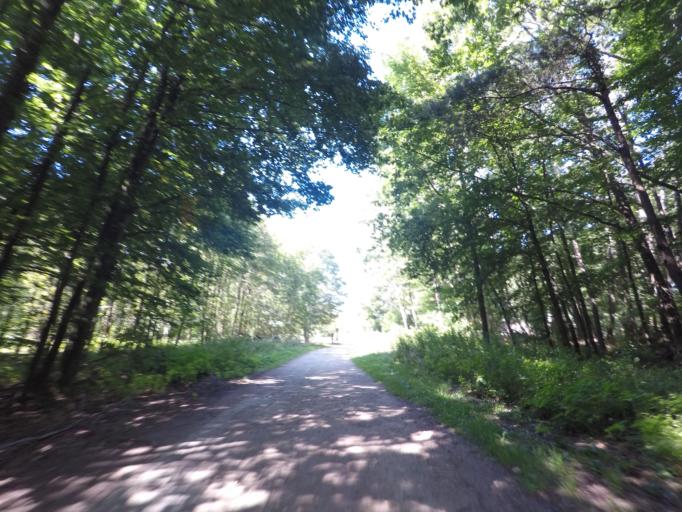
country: LU
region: Luxembourg
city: Bridel
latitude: 49.6462
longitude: 6.0867
